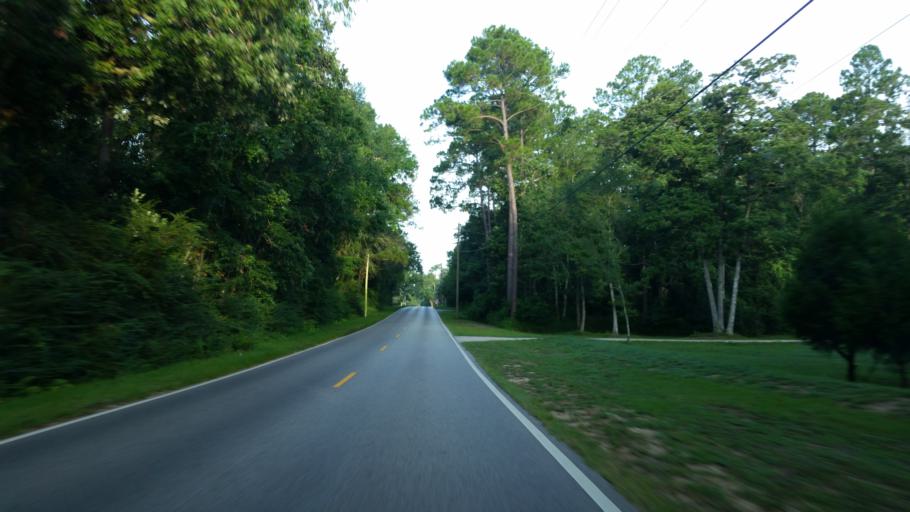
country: US
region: Florida
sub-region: Escambia County
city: Ensley
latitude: 30.5199
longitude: -87.3275
